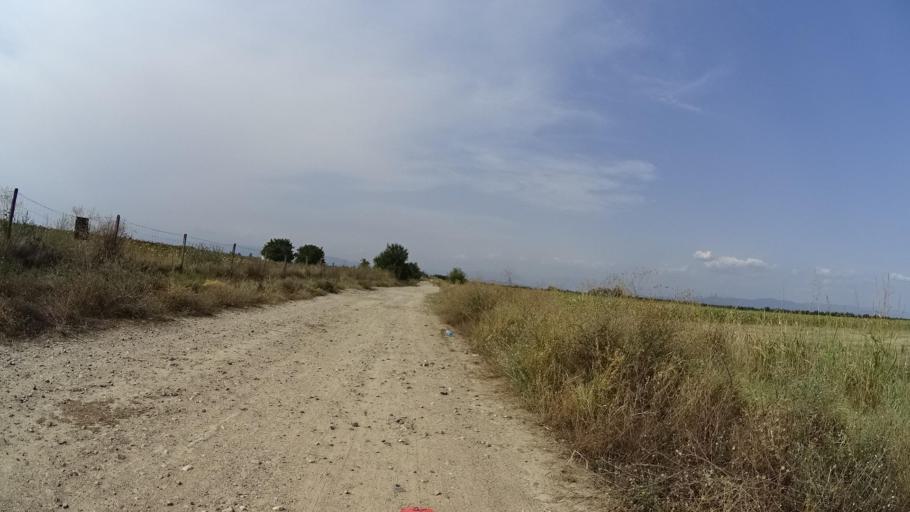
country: BG
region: Plovdiv
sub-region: Obshtina Kaloyanovo
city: Kaloyanovo
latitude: 42.2870
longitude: 24.7973
